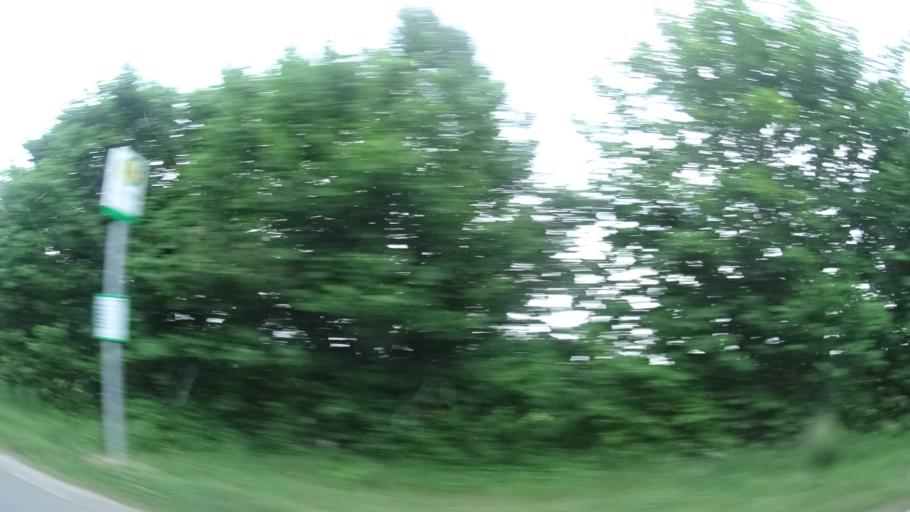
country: DE
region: North Rhine-Westphalia
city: Brakel
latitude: 51.7373
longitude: 9.1700
